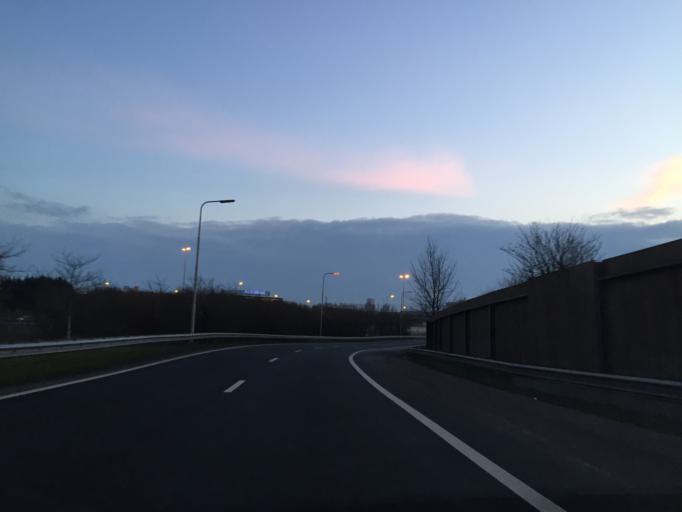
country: NL
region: South Holland
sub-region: Gemeente Leidschendam-Voorburg
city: Voorburg
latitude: 52.0739
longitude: 4.3925
